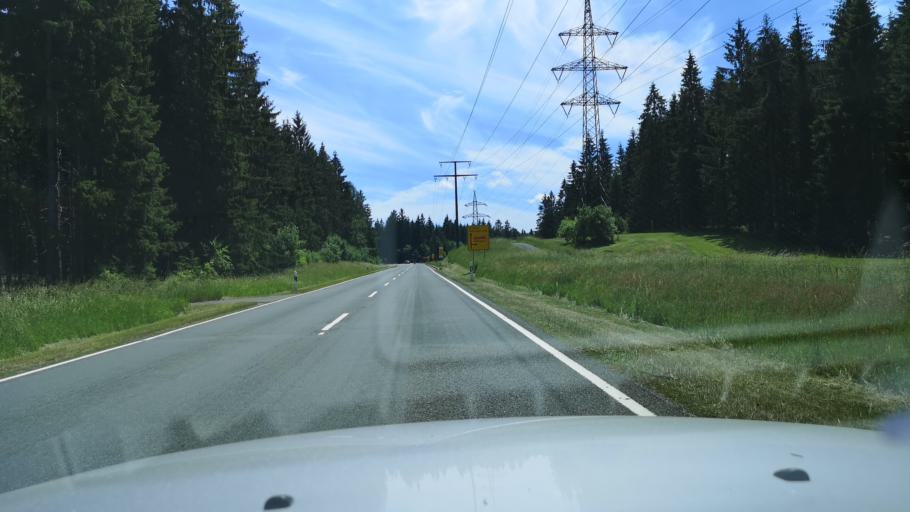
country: DE
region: Thuringia
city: Grafenthal
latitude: 50.4712
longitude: 11.3130
